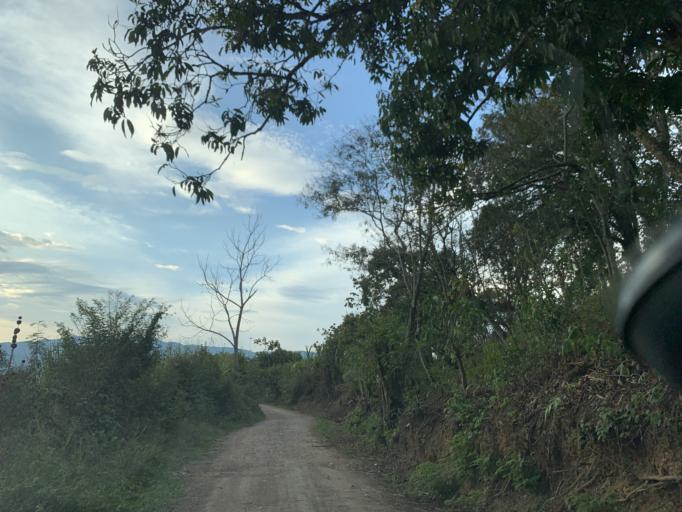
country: CO
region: Boyaca
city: Santana
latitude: 6.0881
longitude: -73.4974
